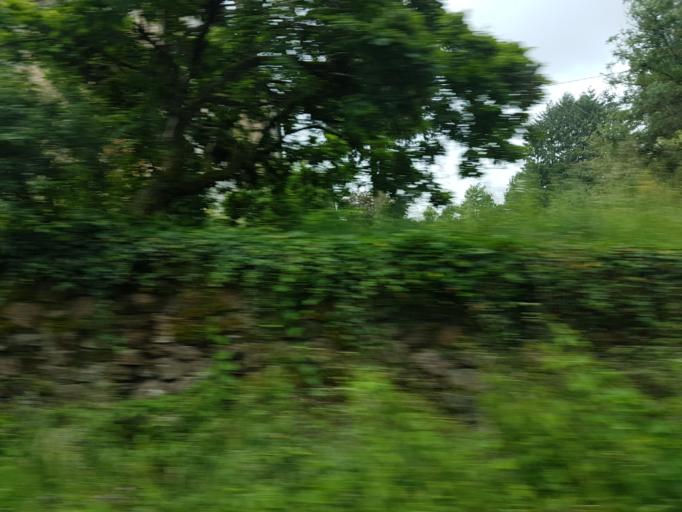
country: FR
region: Bourgogne
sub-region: Departement de la Nievre
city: Lormes
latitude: 47.1643
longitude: 3.8398
